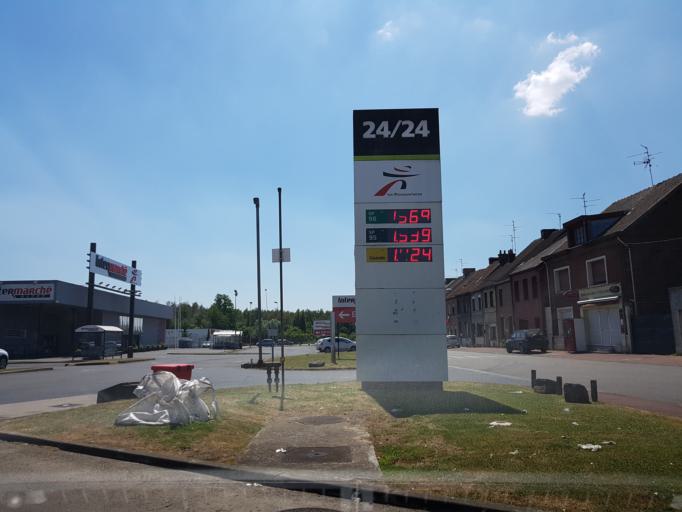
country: FR
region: Nord-Pas-de-Calais
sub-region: Departement du Nord
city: Lourches
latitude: 50.3110
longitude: 3.3459
